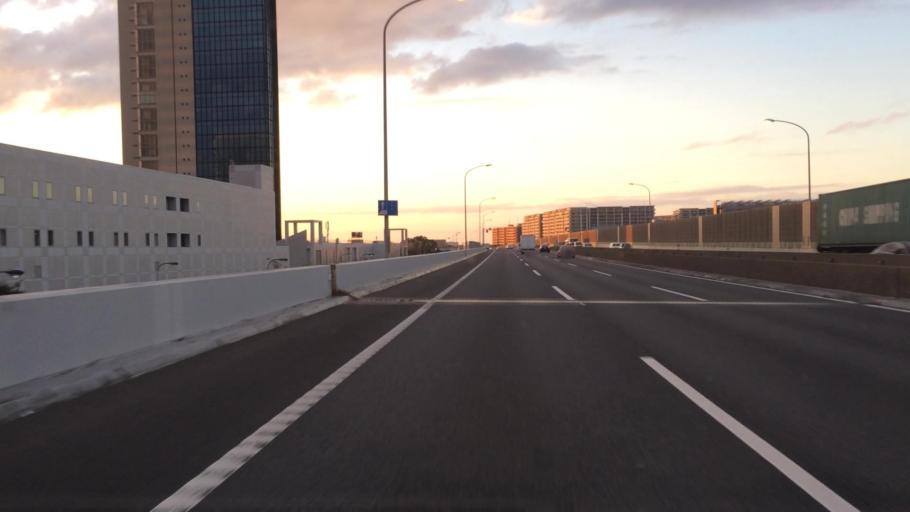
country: JP
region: Chiba
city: Funabashi
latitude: 35.6546
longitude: 140.0427
